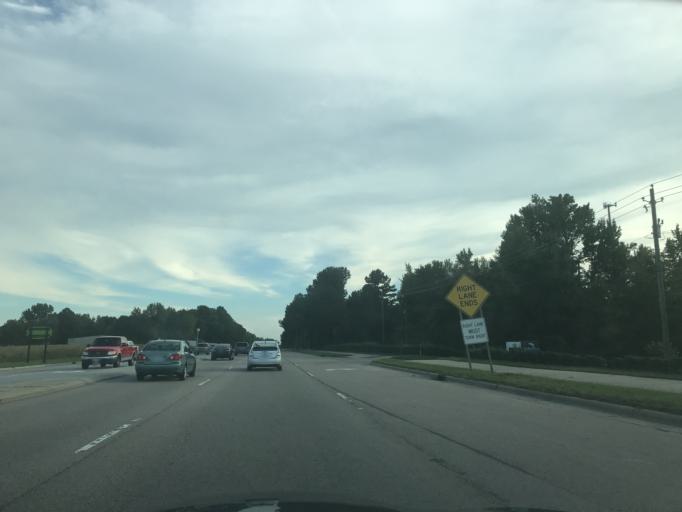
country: US
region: North Carolina
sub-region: Wake County
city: Green Level
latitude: 35.8026
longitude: -78.8714
